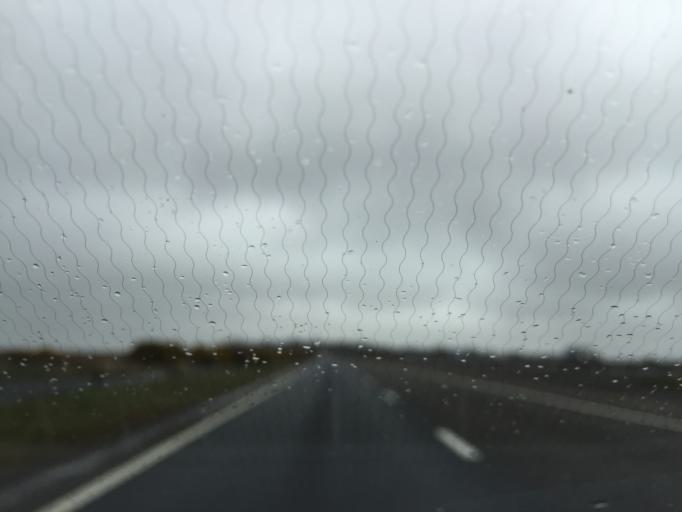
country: GB
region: England
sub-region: Hampshire
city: Bransgore
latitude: 50.8743
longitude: -1.6928
